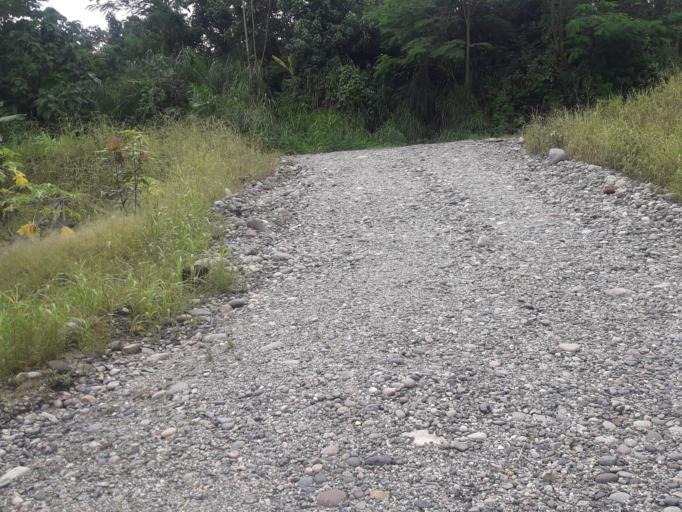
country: EC
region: Napo
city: Tena
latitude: -1.0001
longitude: -77.8080
